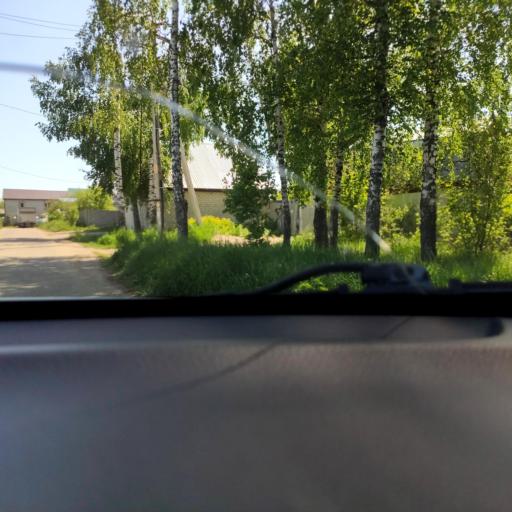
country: RU
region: Tatarstan
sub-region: Gorod Kazan'
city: Kazan
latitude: 55.8606
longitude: 49.1977
